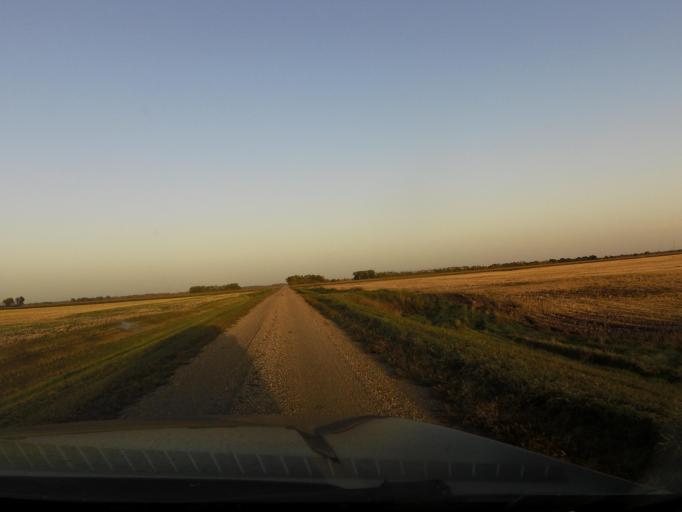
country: US
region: North Dakota
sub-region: Walsh County
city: Grafton
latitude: 48.3832
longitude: -97.2162
